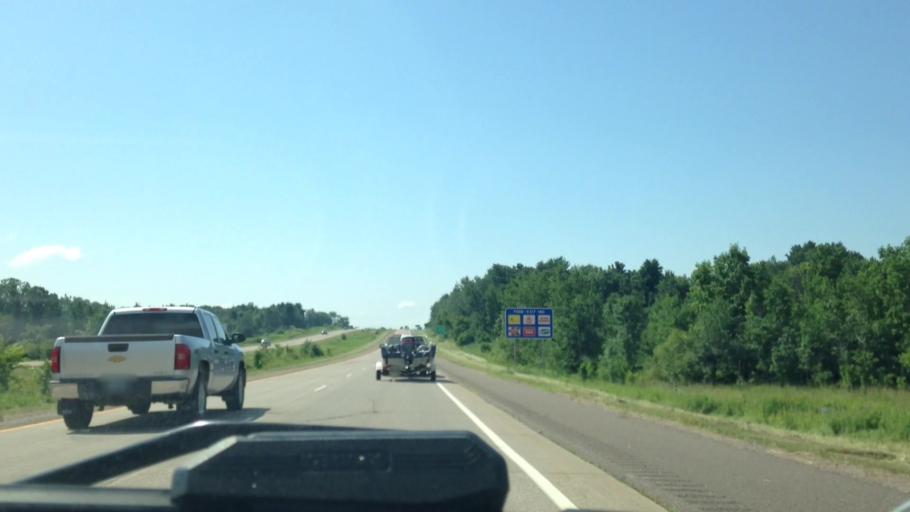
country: US
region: Wisconsin
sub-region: Barron County
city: Rice Lake
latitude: 45.4938
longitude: -91.7640
